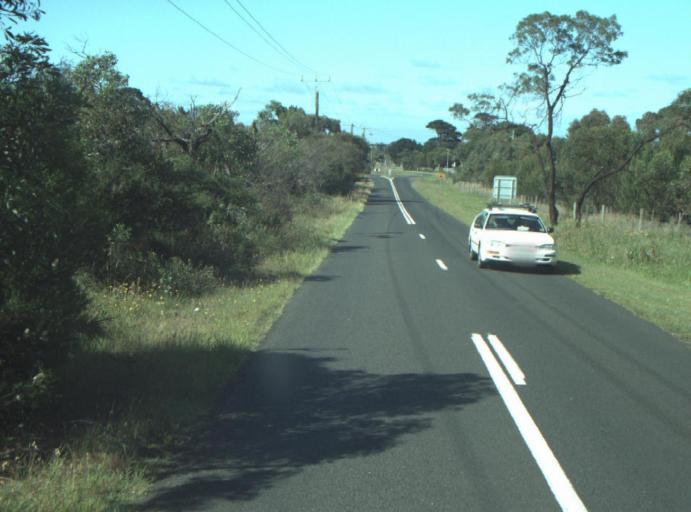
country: AU
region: Victoria
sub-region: Greater Geelong
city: Clifton Springs
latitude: -38.2401
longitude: 144.5743
